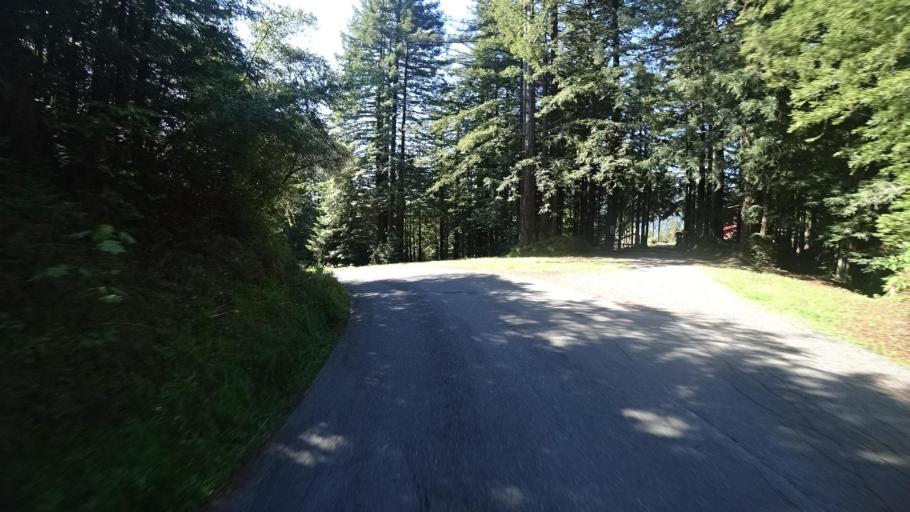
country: US
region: California
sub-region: Humboldt County
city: Rio Dell
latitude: 40.4428
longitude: -123.9720
